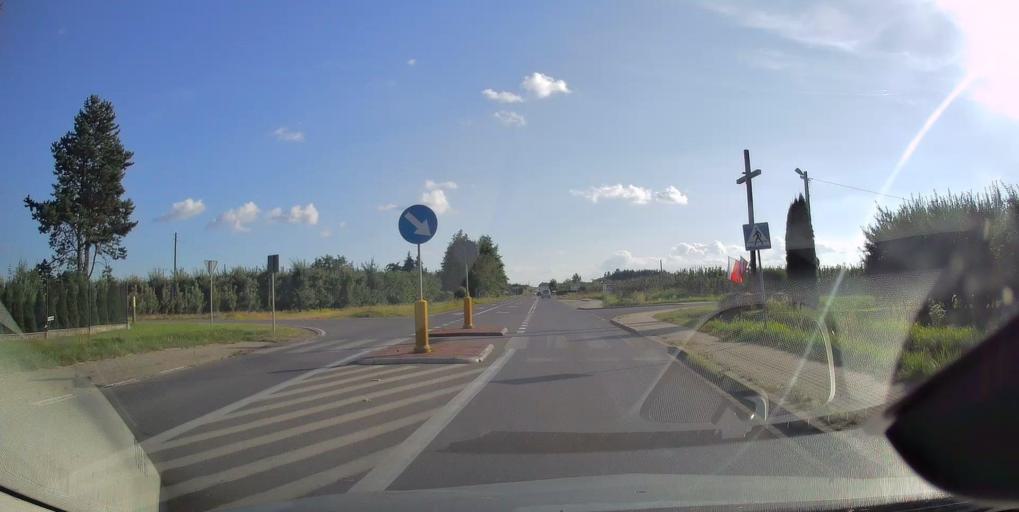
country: PL
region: Masovian Voivodeship
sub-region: Powiat grojecki
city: Belsk Duzy
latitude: 51.8455
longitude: 20.8344
